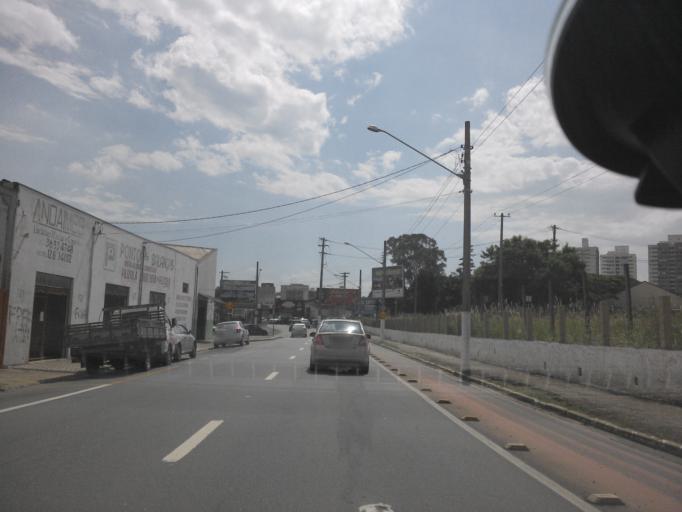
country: BR
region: Sao Paulo
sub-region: Taubate
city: Taubate
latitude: -23.0248
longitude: -45.5666
